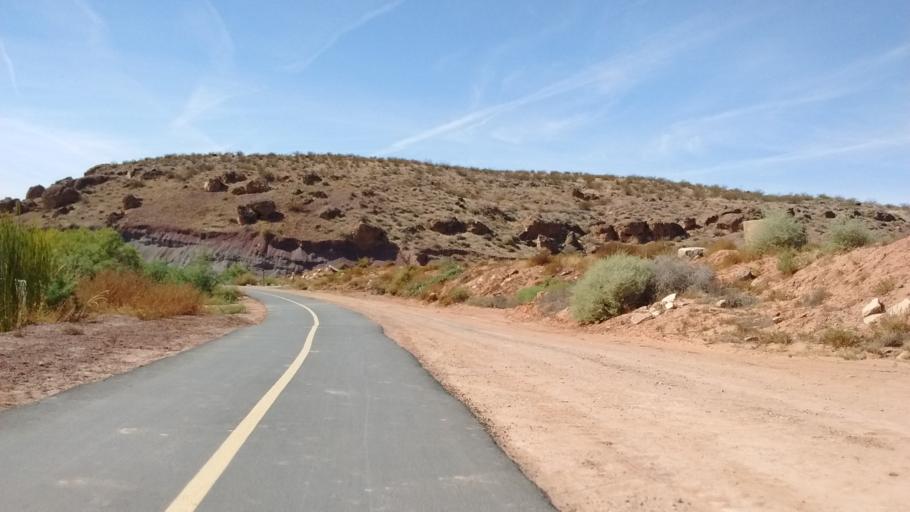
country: US
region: Utah
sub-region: Washington County
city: Washington
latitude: 37.0962
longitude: -113.5362
